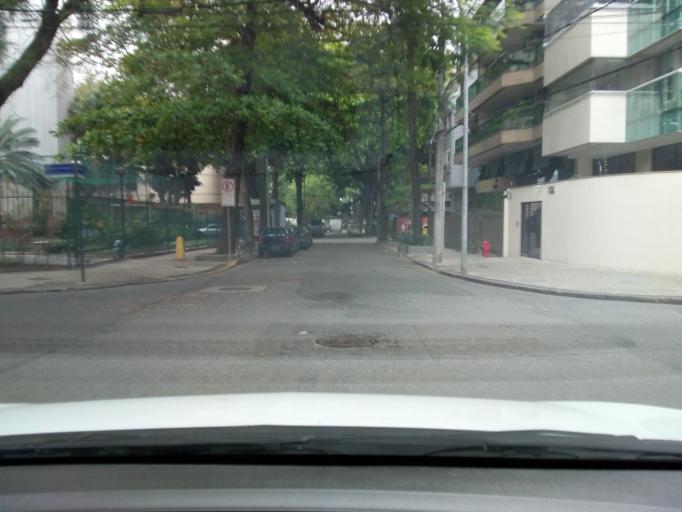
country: BR
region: Rio de Janeiro
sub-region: Rio De Janeiro
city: Rio de Janeiro
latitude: -22.9829
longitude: -43.2245
